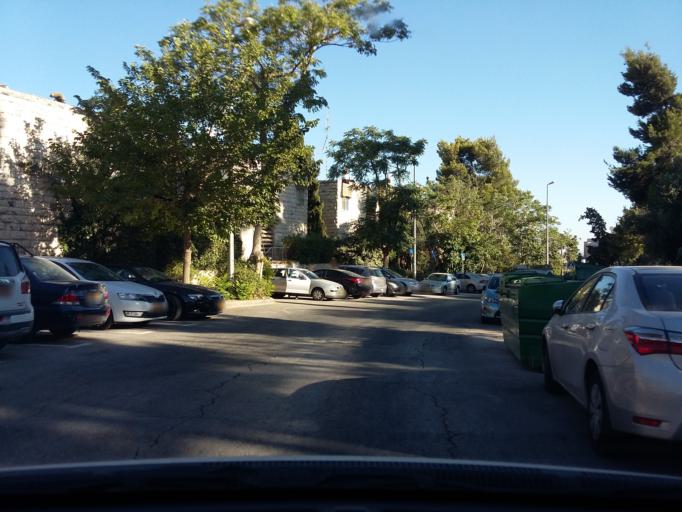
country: PS
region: West Bank
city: `Anata
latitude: 31.8059
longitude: 35.2407
